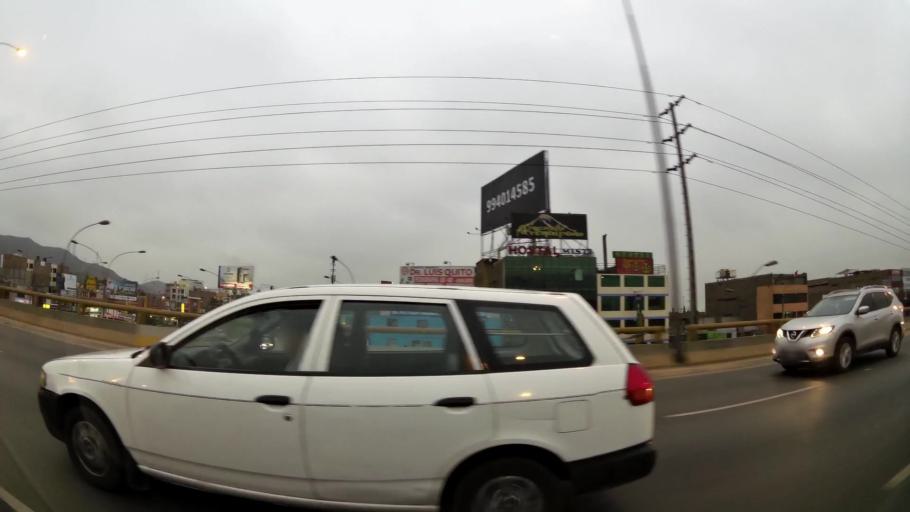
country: PE
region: Lima
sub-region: Lima
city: Independencia
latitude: -11.9897
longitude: -77.0643
